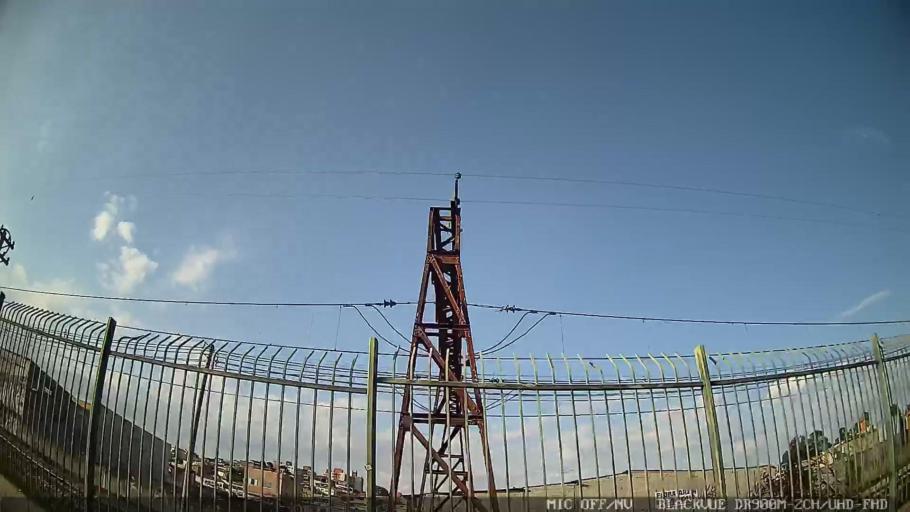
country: BR
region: Sao Paulo
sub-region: Ferraz De Vasconcelos
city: Ferraz de Vasconcelos
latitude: -23.5450
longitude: -46.4064
